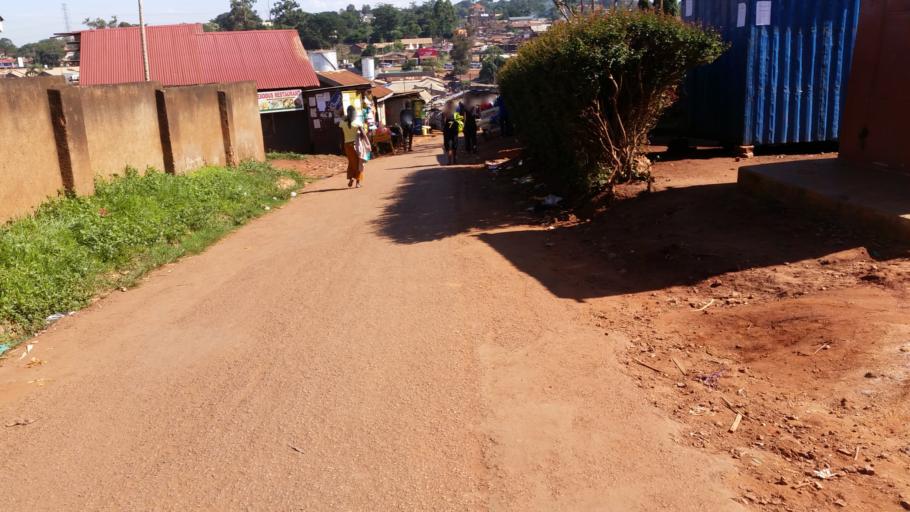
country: UG
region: Central Region
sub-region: Wakiso District
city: Kireka
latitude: 0.3400
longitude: 32.6377
